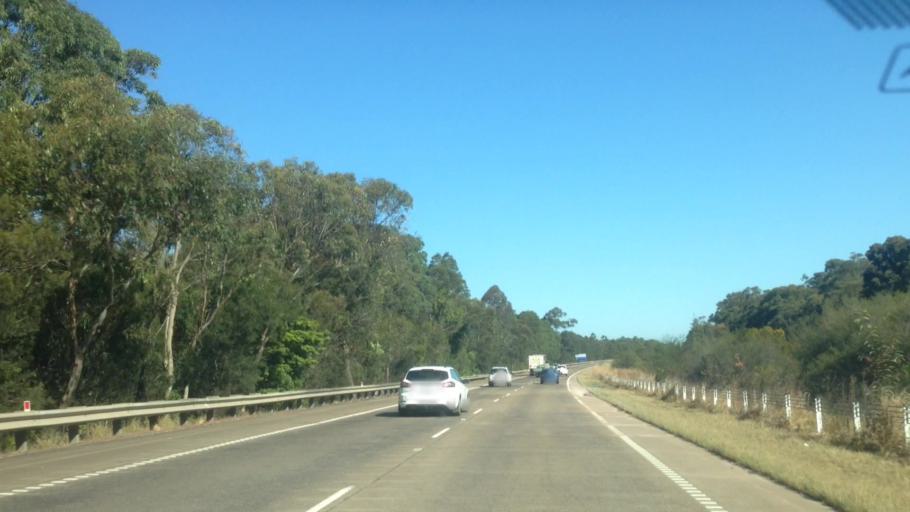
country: AU
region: New South Wales
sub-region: Wyong Shire
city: Charmhaven
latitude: -33.1856
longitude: 151.4680
